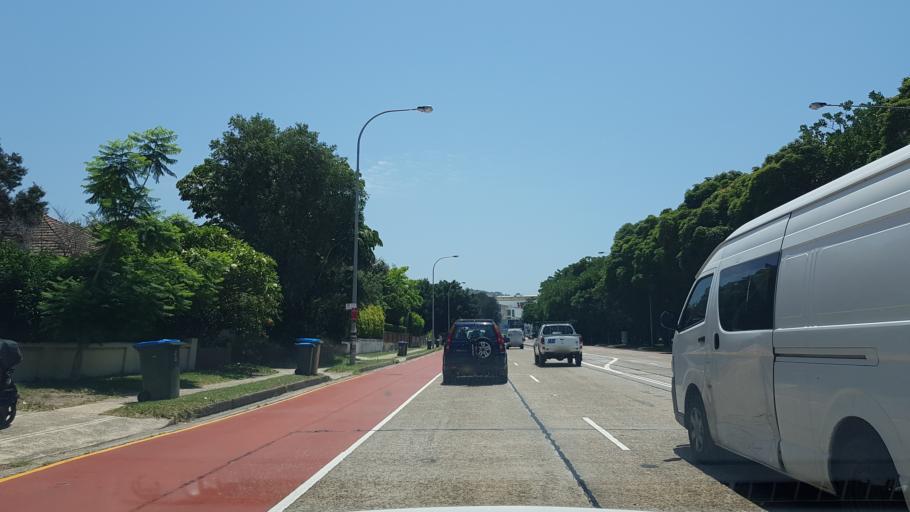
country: AU
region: New South Wales
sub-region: Warringah
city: North Manly
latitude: -33.7731
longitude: 151.2659
